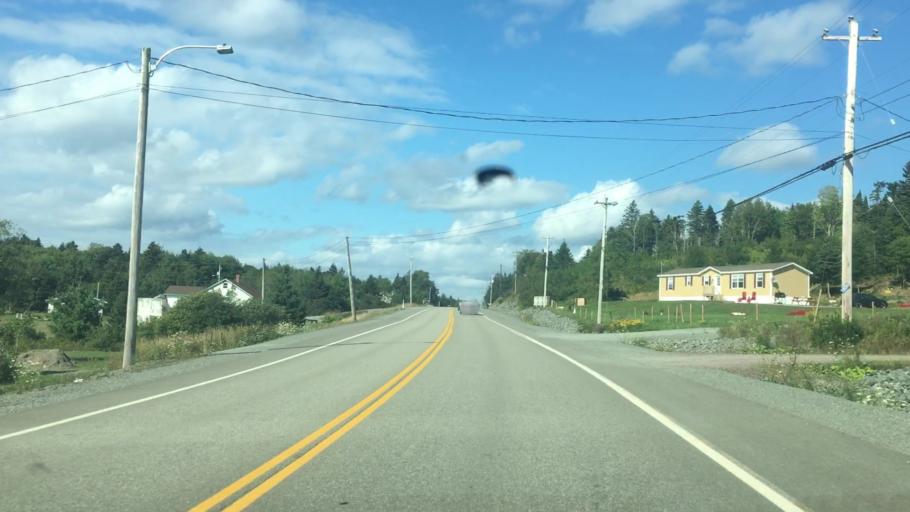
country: CA
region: Nova Scotia
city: Princeville
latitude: 45.6862
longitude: -60.7542
